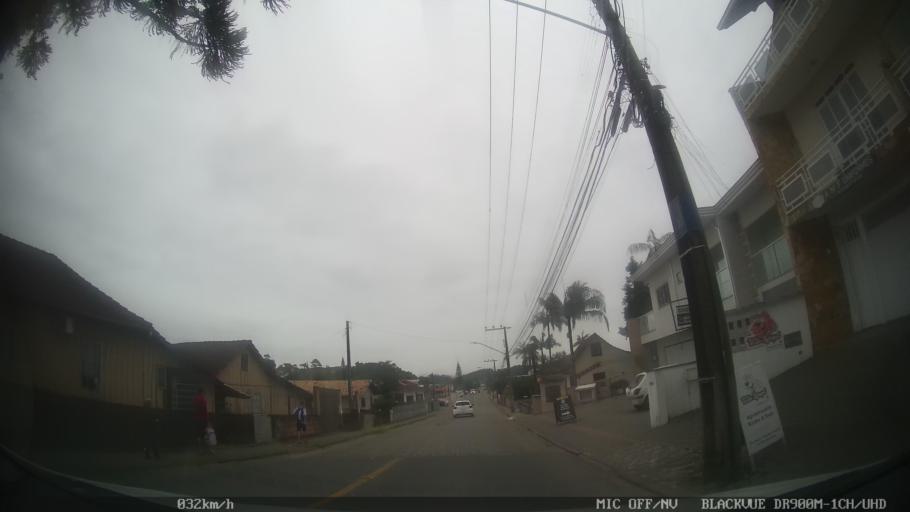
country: BR
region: Santa Catarina
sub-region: Joinville
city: Joinville
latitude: -26.3430
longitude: -48.8477
